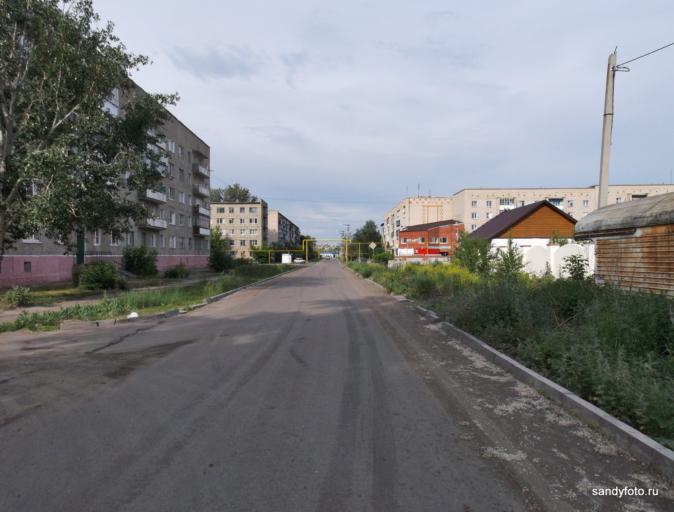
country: RU
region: Chelyabinsk
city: Troitsk
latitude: 54.0908
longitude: 61.5490
